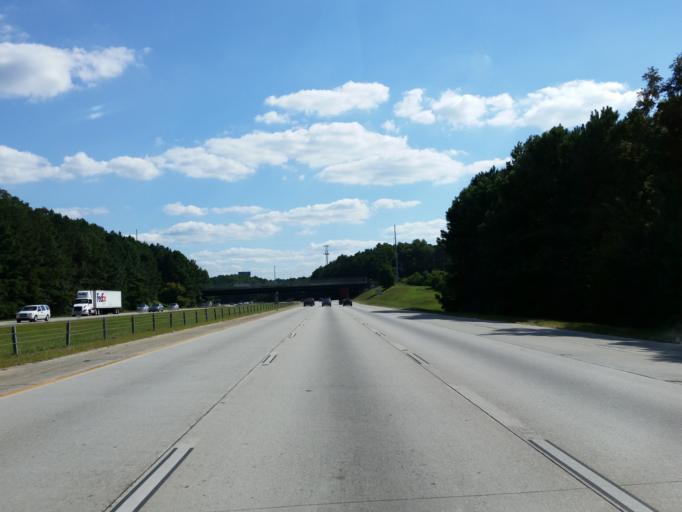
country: US
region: Georgia
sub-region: Clayton County
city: Conley
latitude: 33.6616
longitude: -84.3252
